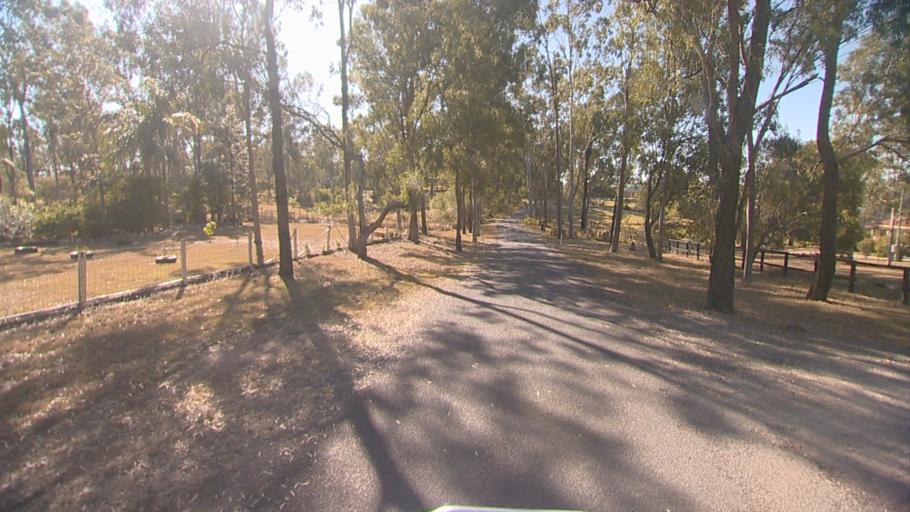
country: AU
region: Queensland
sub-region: Logan
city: Cedar Vale
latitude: -27.8567
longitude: 153.0318
